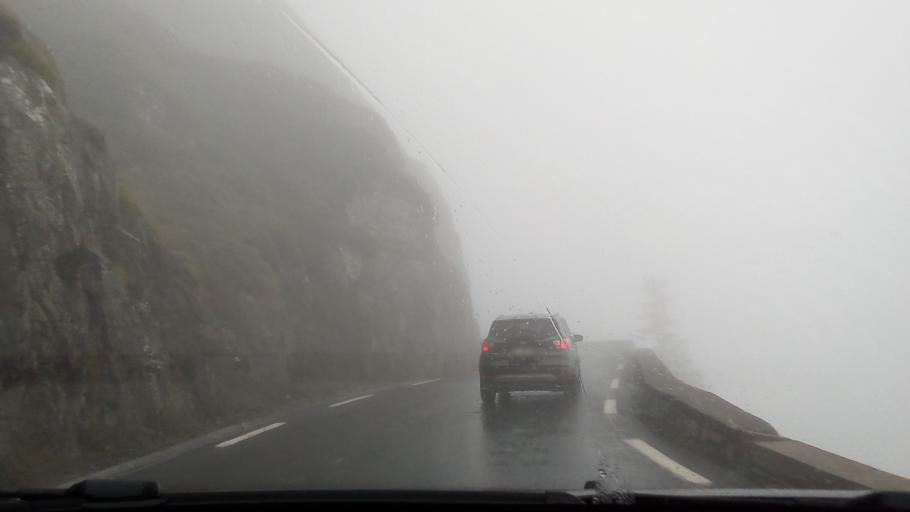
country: FR
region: Midi-Pyrenees
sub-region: Departement des Hautes-Pyrenees
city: Campan
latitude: 42.9100
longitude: 0.1394
